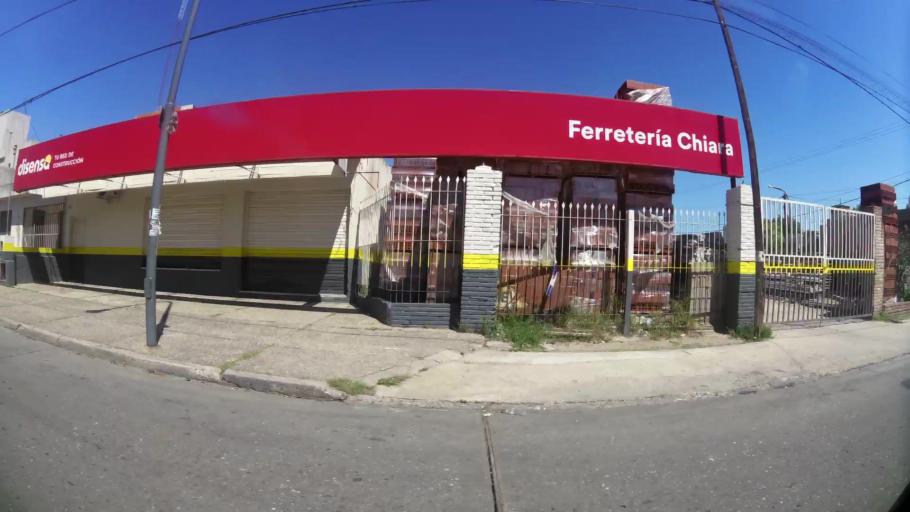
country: AR
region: Cordoba
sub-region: Departamento de Capital
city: Cordoba
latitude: -31.4225
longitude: -64.2092
